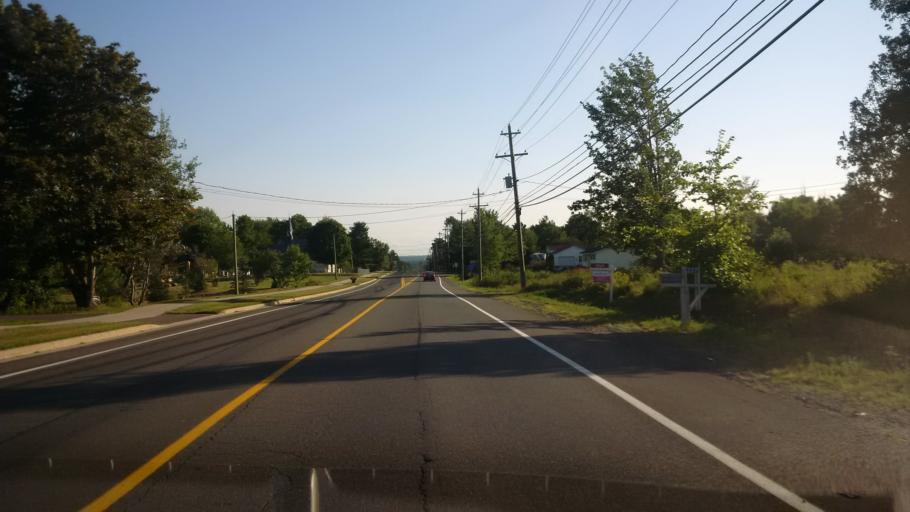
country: CA
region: New Brunswick
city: Fredericton
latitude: 45.8924
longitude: -66.6838
